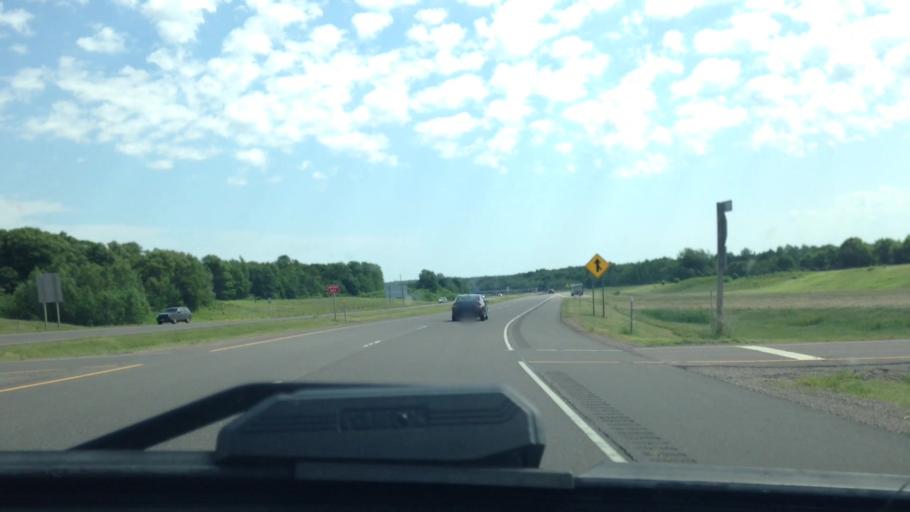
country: US
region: Wisconsin
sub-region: Washburn County
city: Spooner
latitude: 45.8562
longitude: -91.8561
